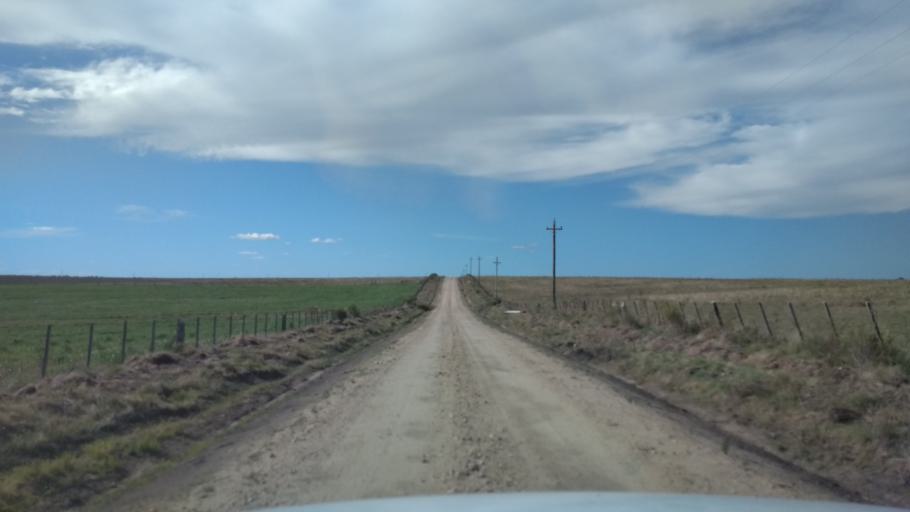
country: UY
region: Florida
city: Casupa
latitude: -34.0091
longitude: -55.7870
